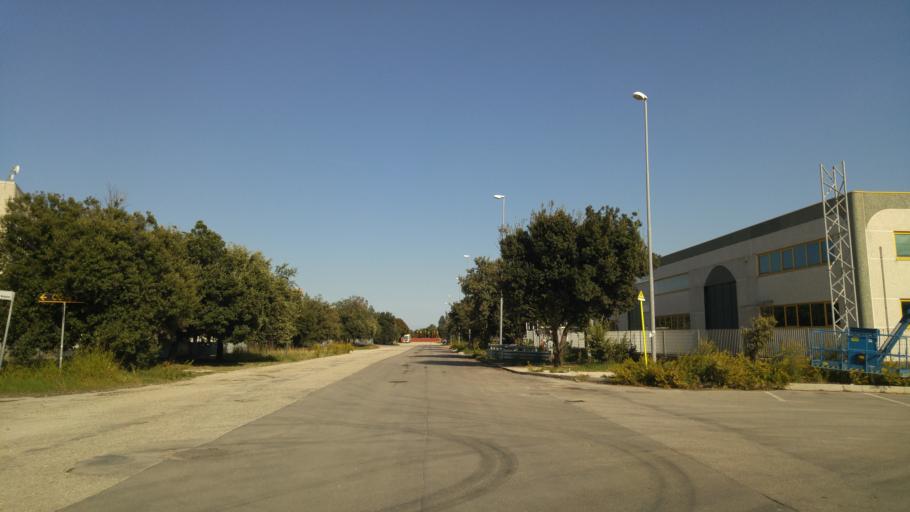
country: IT
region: The Marches
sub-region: Provincia di Pesaro e Urbino
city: Bellocchi
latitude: 43.7941
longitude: 13.0119
